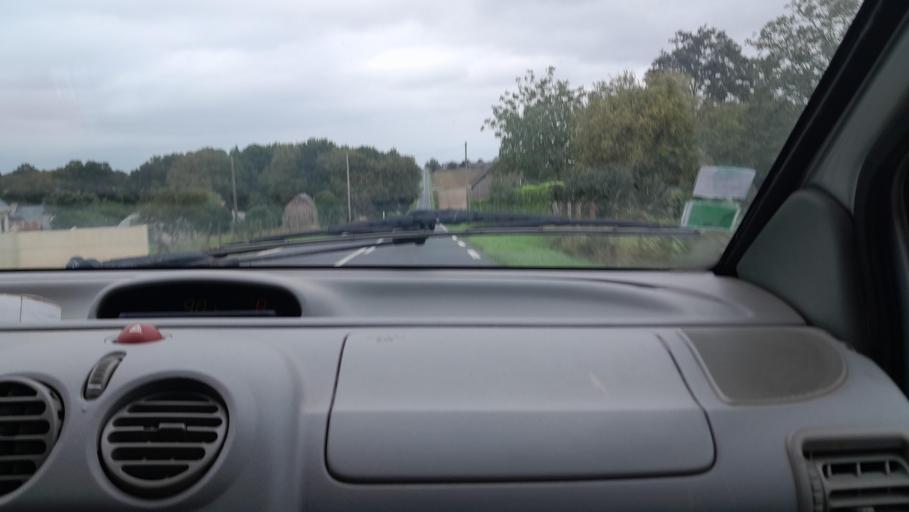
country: FR
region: Pays de la Loire
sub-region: Departement de la Loire-Atlantique
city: Saint-Mars-la-Jaille
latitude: 47.5456
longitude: -1.1861
